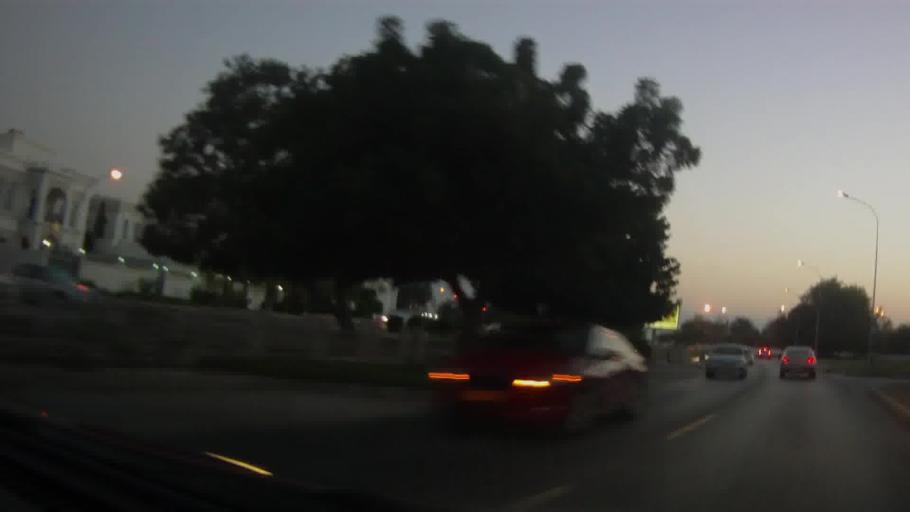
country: OM
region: Muhafazat Masqat
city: Bawshar
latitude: 23.6057
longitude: 58.4433
